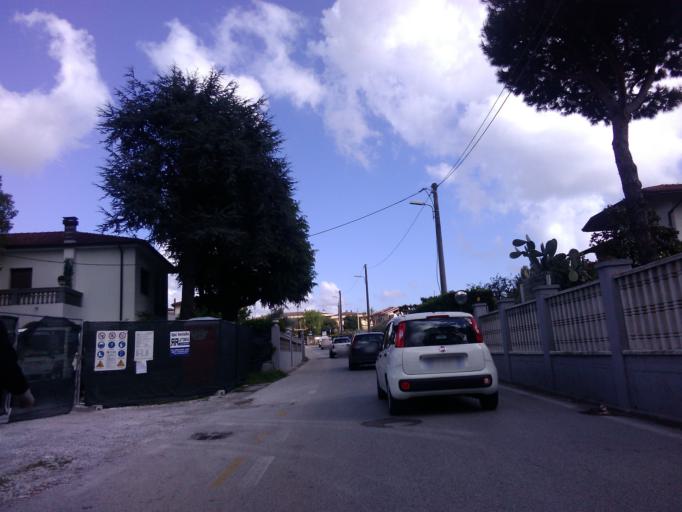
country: IT
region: Tuscany
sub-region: Provincia di Massa-Carrara
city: Massa
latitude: 44.0220
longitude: 10.1229
